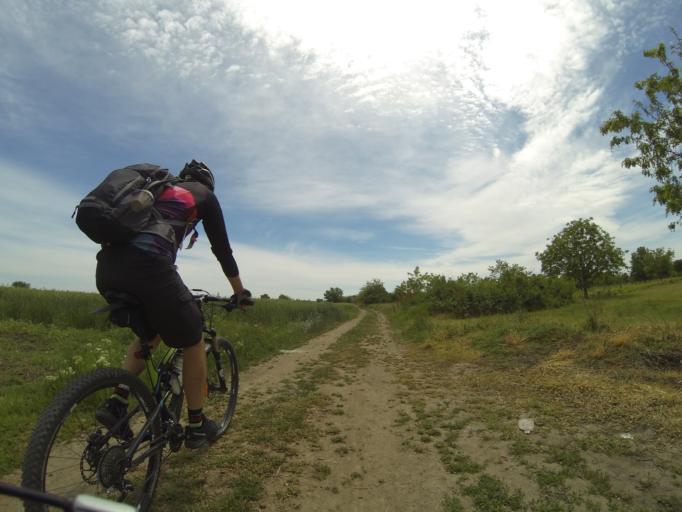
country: RO
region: Dolj
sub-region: Comuna Leu
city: Leu
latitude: 44.2006
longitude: 24.0005
